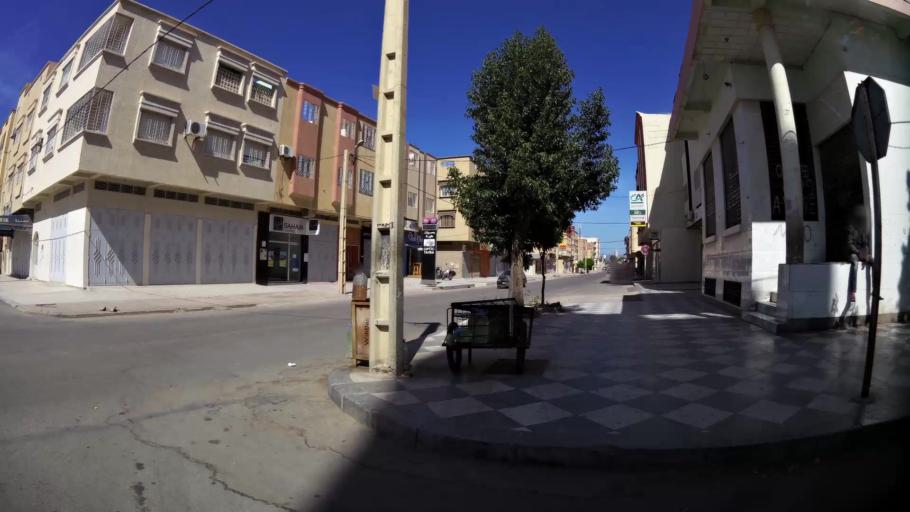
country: MA
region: Oriental
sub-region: Oujda-Angad
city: Oujda
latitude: 34.6580
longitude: -1.9168
